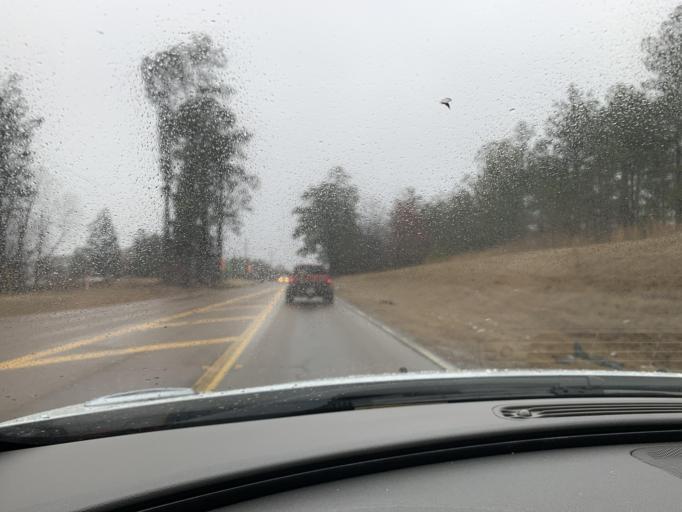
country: US
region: Mississippi
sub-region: De Soto County
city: Horn Lake
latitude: 34.9236
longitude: -90.0090
